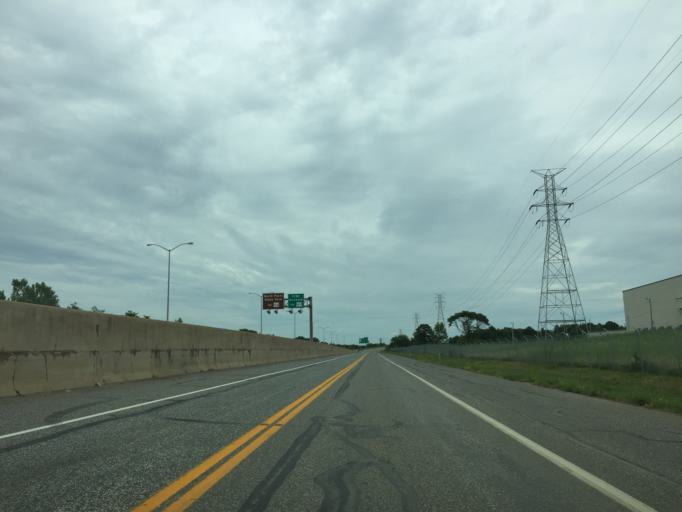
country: US
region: Maryland
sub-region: Baltimore County
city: Dundalk
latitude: 39.2380
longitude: -76.4864
